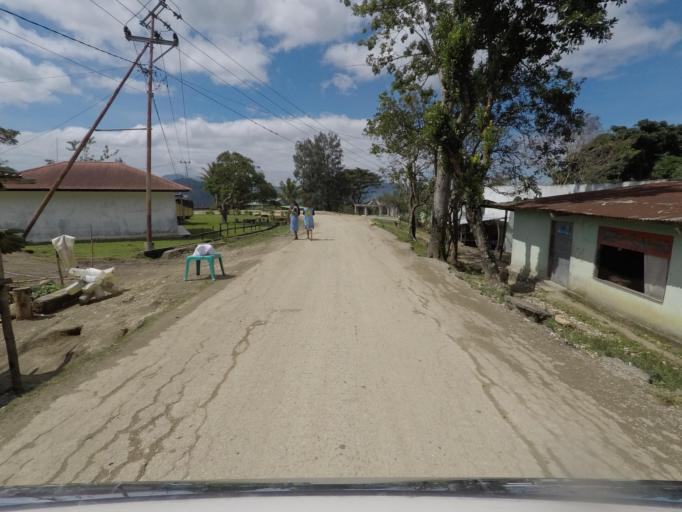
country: TL
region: Baucau
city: Venilale
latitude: -8.7401
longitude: 126.3747
